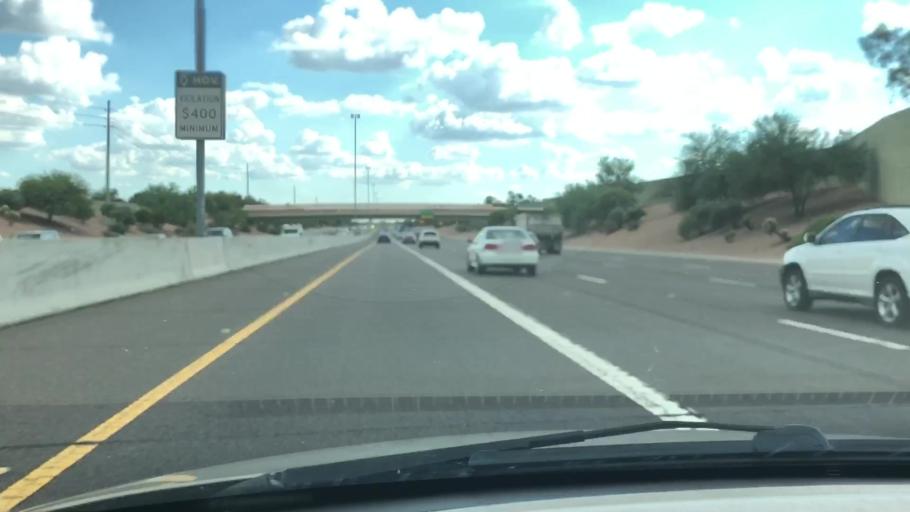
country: US
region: Arizona
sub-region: Maricopa County
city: Paradise Valley
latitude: 33.6069
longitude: -111.8918
